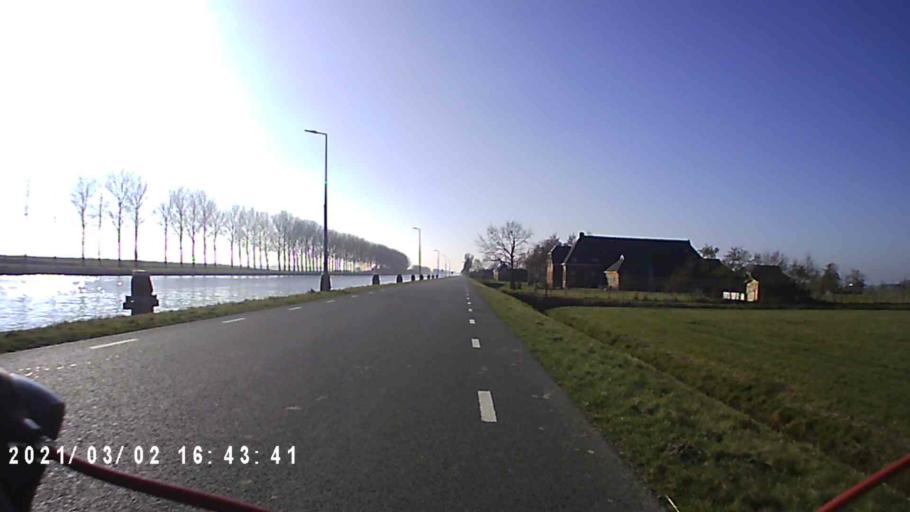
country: NL
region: Groningen
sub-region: Gemeente Zuidhorn
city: Grijpskerk
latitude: 53.2484
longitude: 6.3036
